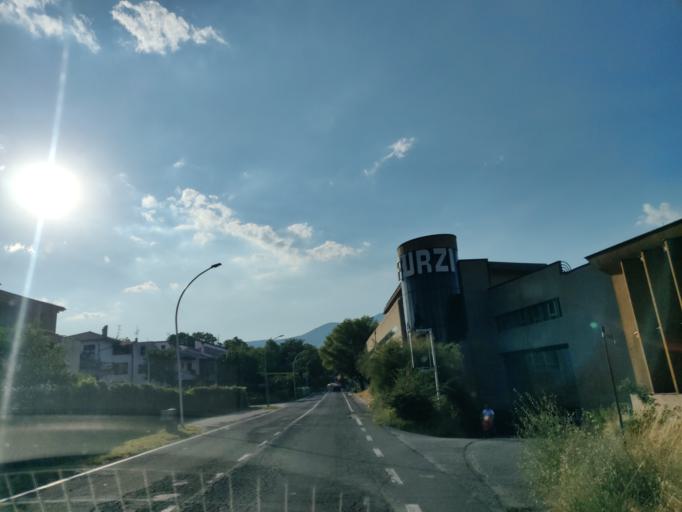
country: IT
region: Tuscany
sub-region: Provincia di Siena
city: Piancastagnaio
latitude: 42.8522
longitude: 11.6875
